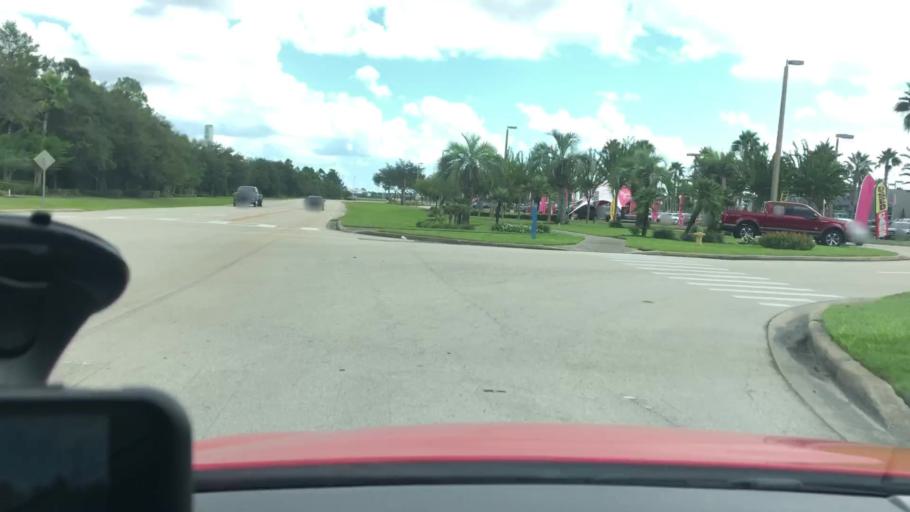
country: US
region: Florida
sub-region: Volusia County
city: Holly Hill
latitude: 29.2165
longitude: -81.1064
